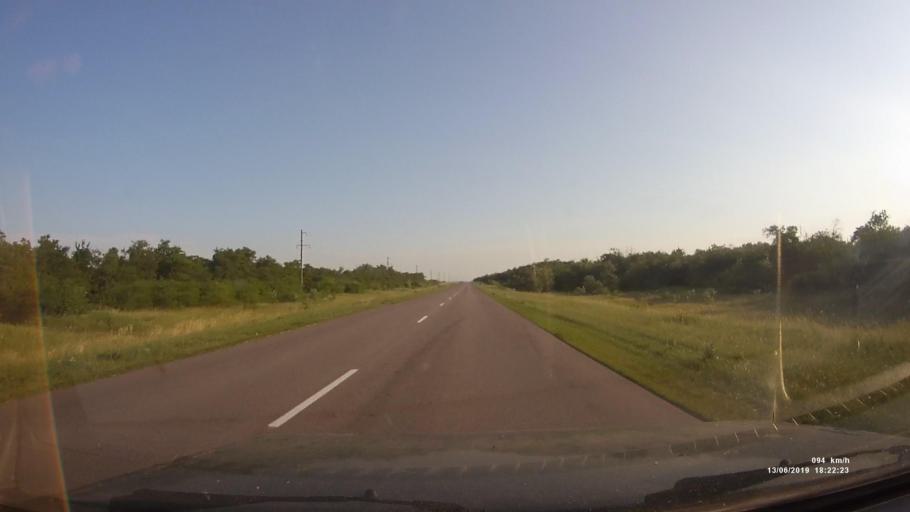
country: RU
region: Rostov
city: Kazanskaya
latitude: 49.8591
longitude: 41.2790
